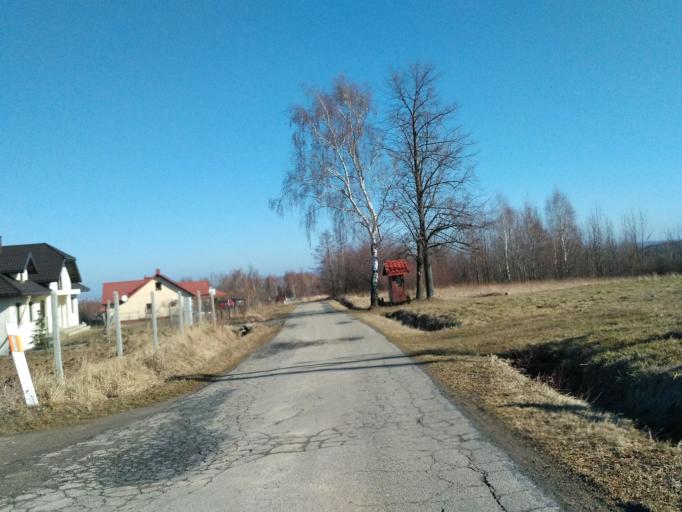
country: PL
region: Subcarpathian Voivodeship
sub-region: Powiat rzeszowski
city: Siedliska
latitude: 49.9414
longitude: 21.9489
